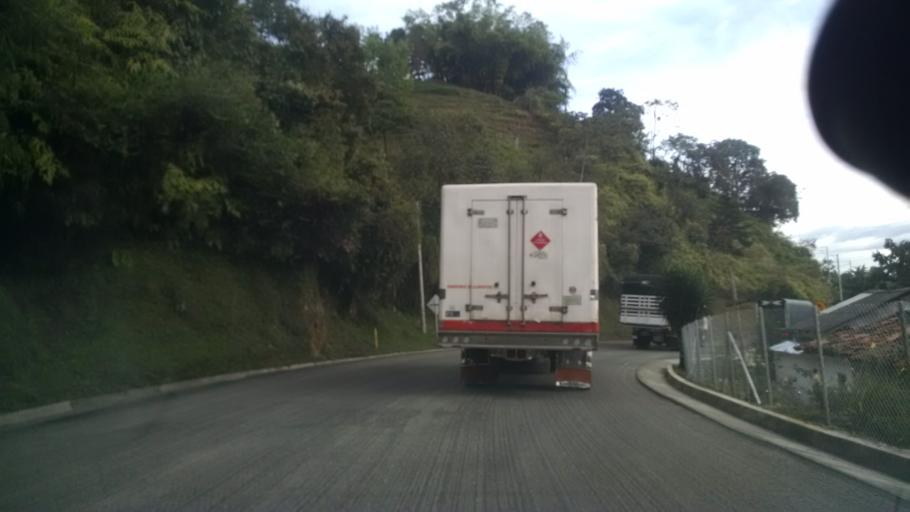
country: CO
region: Antioquia
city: Santa Barbara
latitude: 5.9035
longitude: -75.5746
